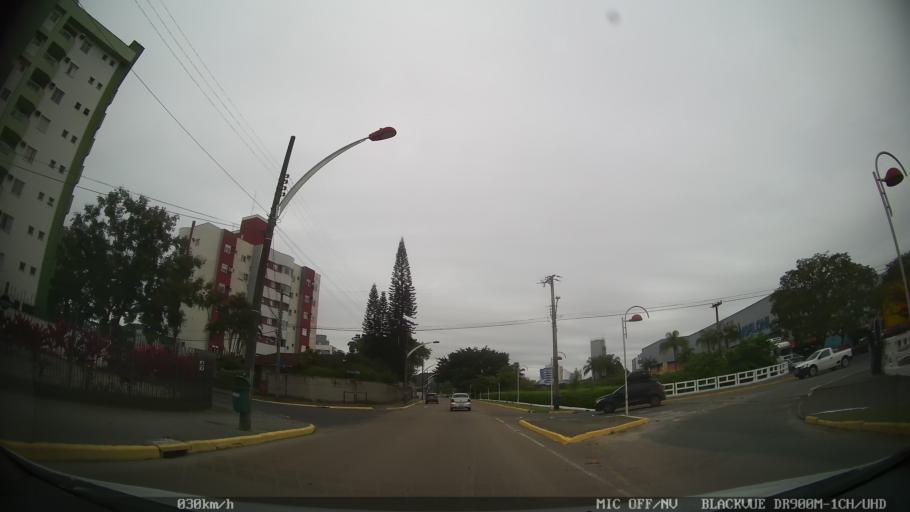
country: BR
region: Santa Catarina
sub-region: Joinville
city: Joinville
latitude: -26.2773
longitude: -48.8484
